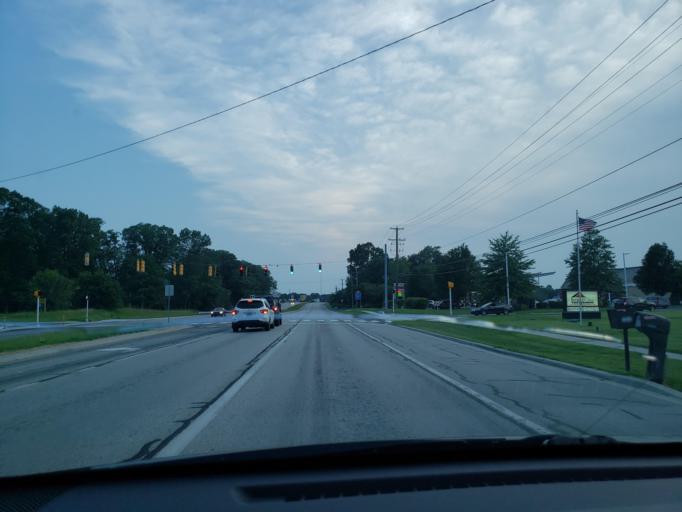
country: US
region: Delaware
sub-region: Kent County
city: Dover Base Housing
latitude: 39.1237
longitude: -75.4998
